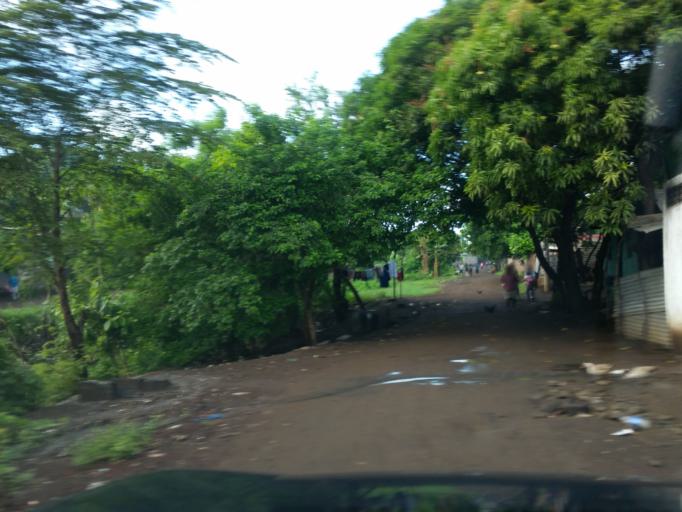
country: NI
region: Managua
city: Managua
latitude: 12.1110
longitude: -86.2043
